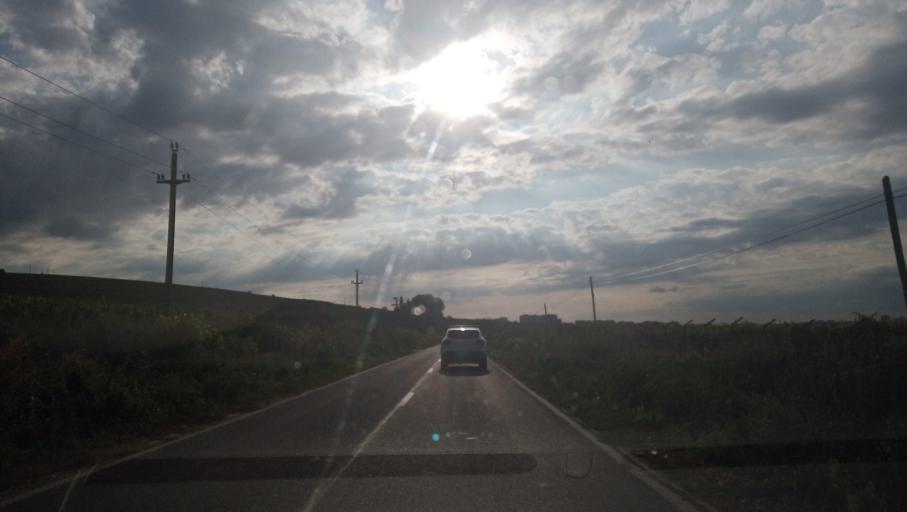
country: BG
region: Silistra
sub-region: Obshtina Silistra
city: Silistra
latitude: 44.1071
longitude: 27.3017
